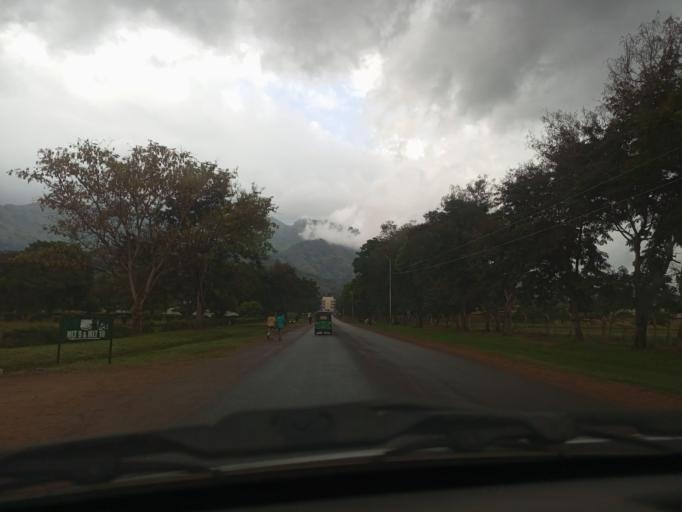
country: TZ
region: Morogoro
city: Morogoro
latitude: -6.8468
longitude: 37.6577
